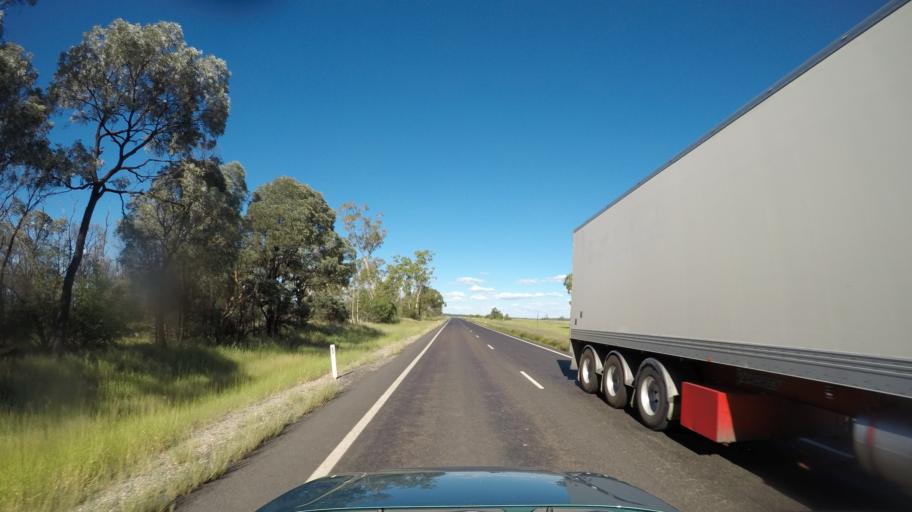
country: AU
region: Queensland
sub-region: Goondiwindi
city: Goondiwindi
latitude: -28.1539
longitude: 150.6768
